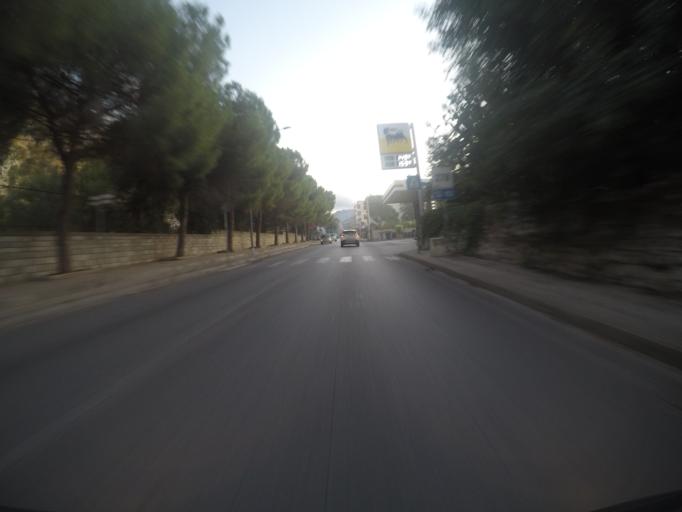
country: IT
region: Sicily
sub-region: Palermo
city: Capaci
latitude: 38.1781
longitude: 13.2438
